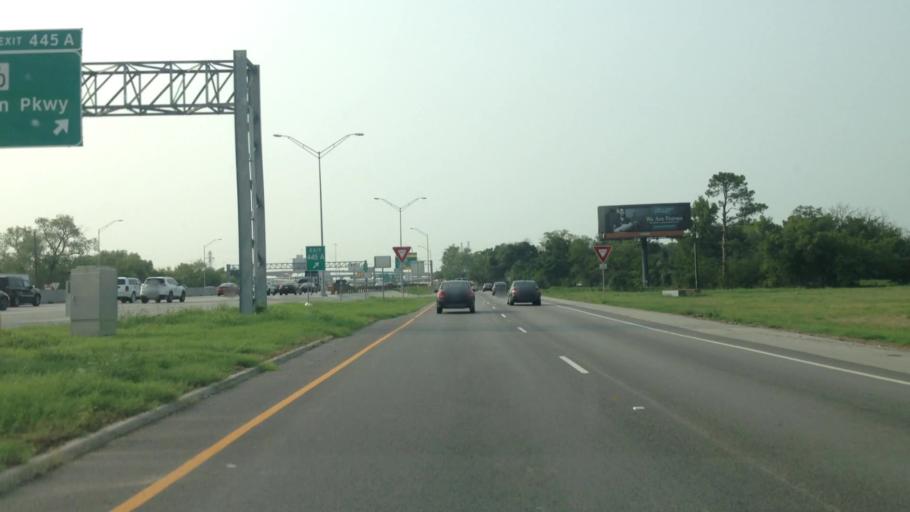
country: US
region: Texas
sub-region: Dallas County
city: Carrollton
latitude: 32.9707
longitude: -96.9203
